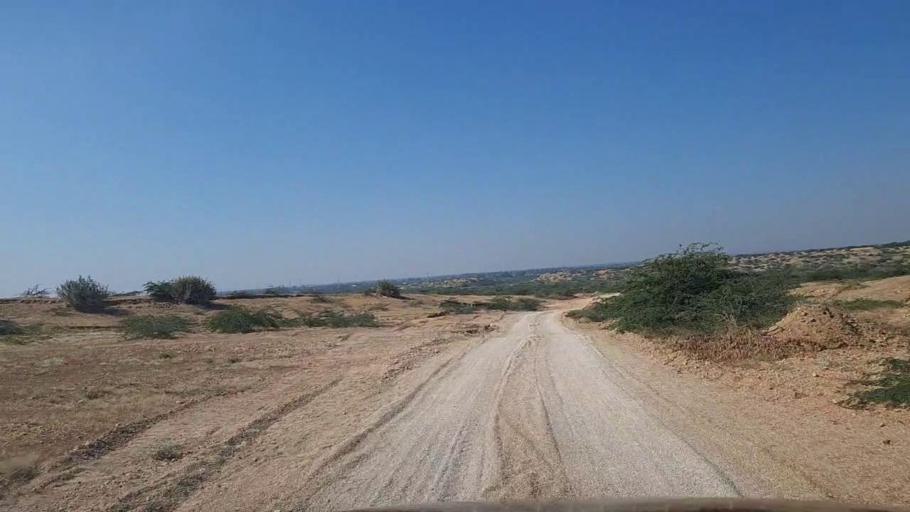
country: PK
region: Sindh
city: Thatta
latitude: 24.6221
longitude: 67.8487
